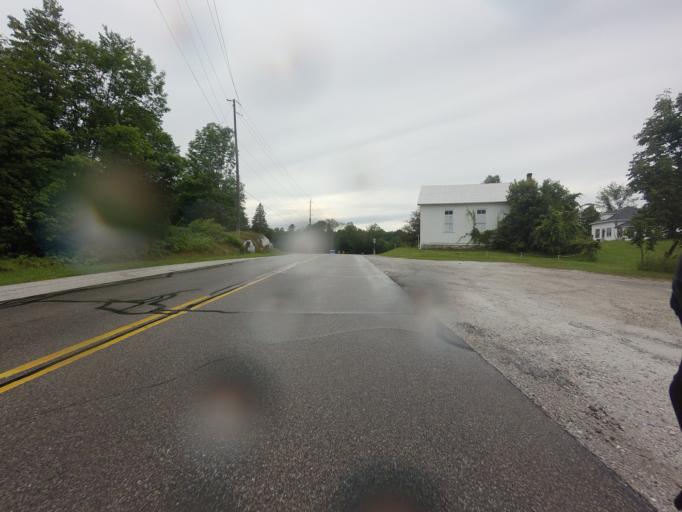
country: CA
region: Ontario
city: Perth
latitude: 44.9674
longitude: -76.4088
